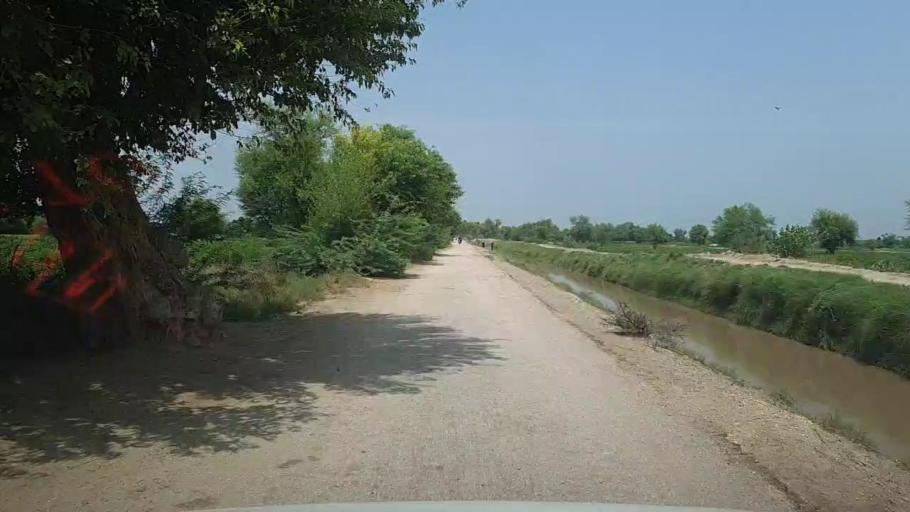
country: PK
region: Sindh
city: Karaundi
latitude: 26.8991
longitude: 68.3314
